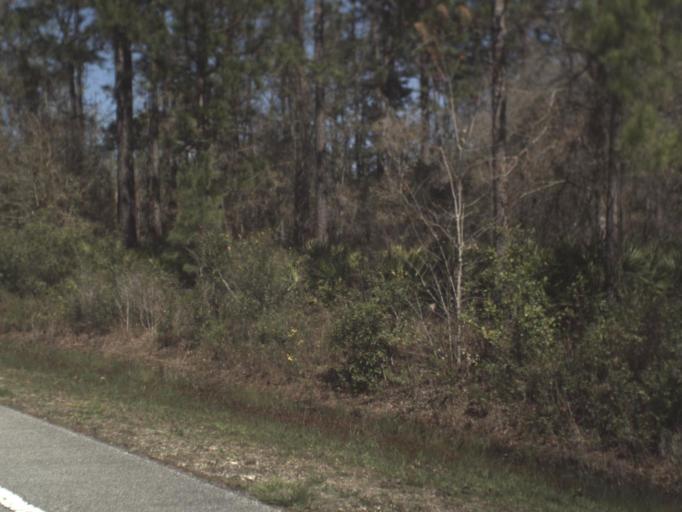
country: US
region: Florida
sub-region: Leon County
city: Woodville
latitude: 30.1810
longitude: -84.2124
